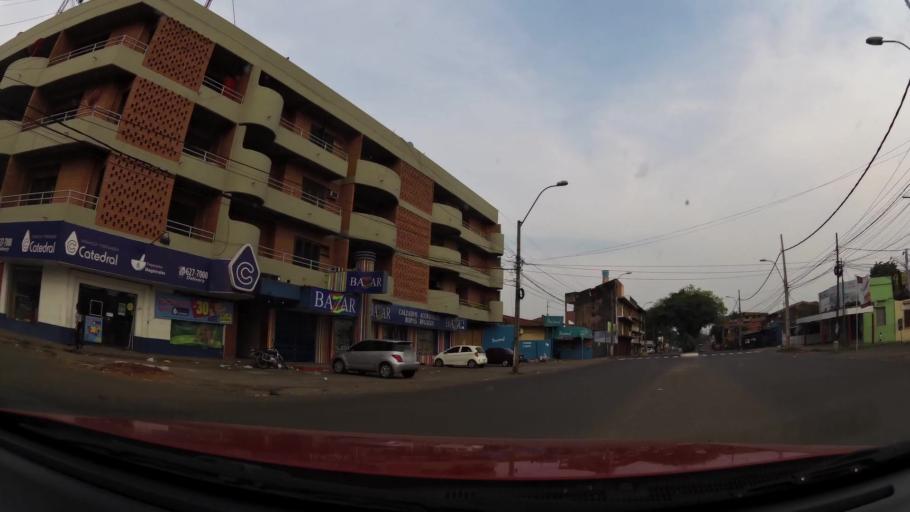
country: PY
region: Asuncion
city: Asuncion
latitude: -25.3098
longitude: -57.6143
